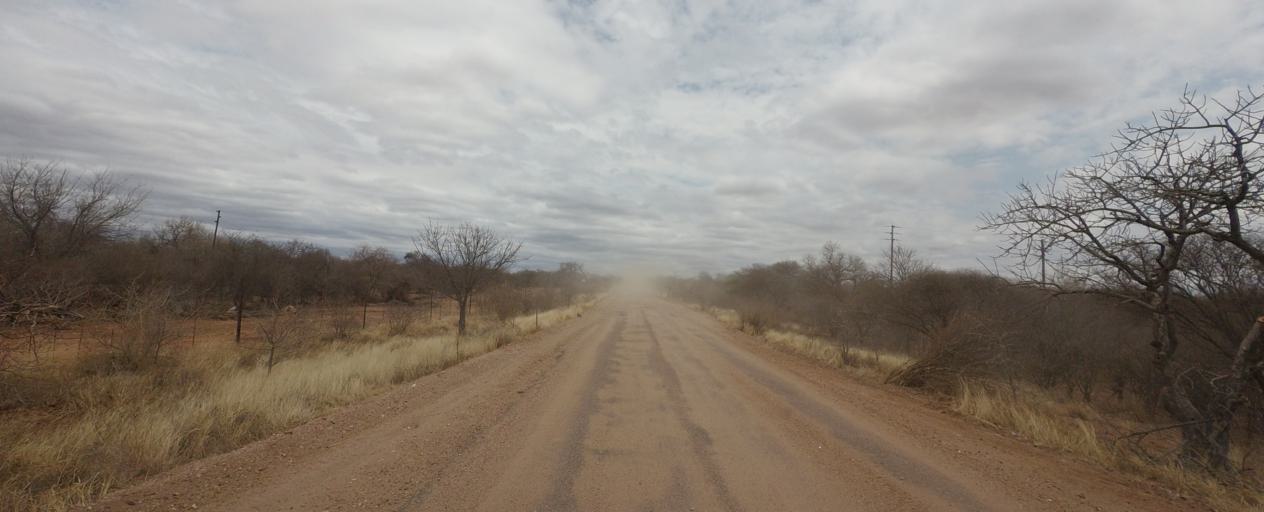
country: BW
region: Central
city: Mathathane
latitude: -22.6759
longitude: 28.6712
